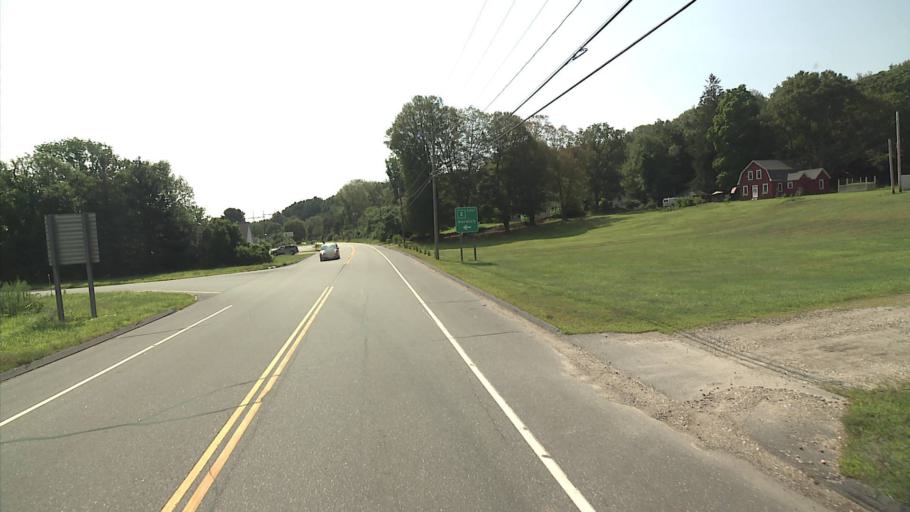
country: US
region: Connecticut
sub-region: New London County
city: Baltic
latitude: 41.5652
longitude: -72.1431
